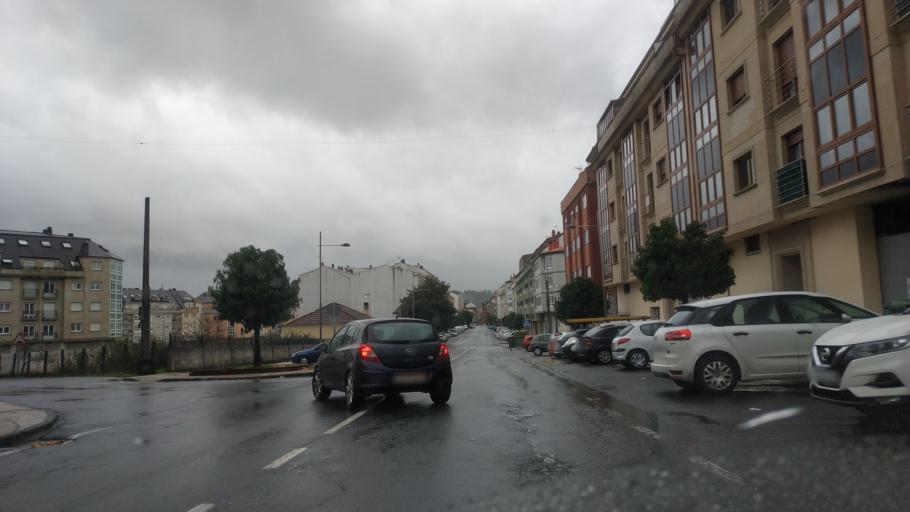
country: ES
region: Galicia
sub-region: Provincia da Coruna
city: Negreira
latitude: 42.9152
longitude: -8.7354
